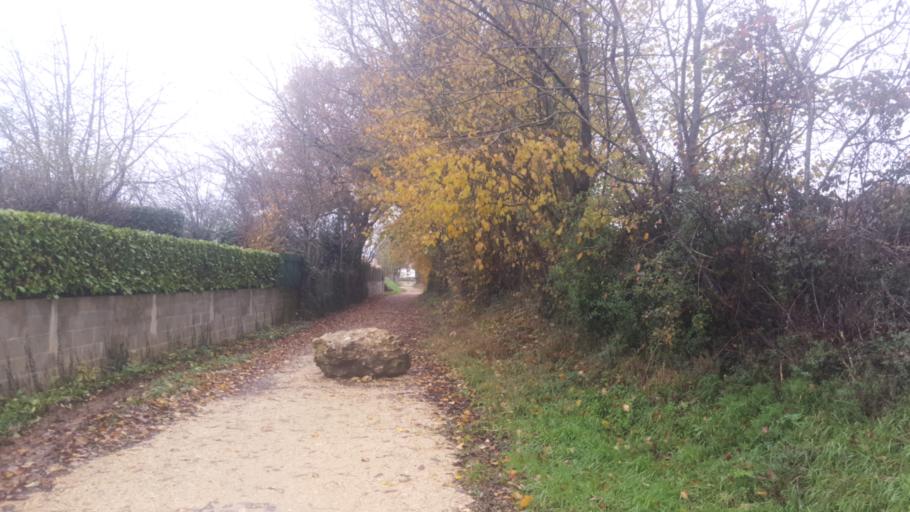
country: FR
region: Poitou-Charentes
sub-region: Departement des Deux-Sevres
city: Melle
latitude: 46.2317
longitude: -0.1336
